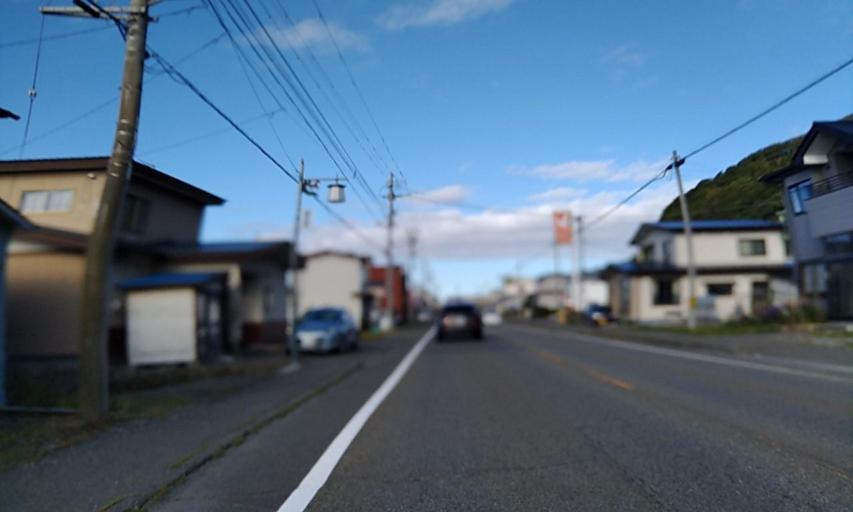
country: JP
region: Hokkaido
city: Shizunai-furukawacho
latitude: 42.2510
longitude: 142.5472
